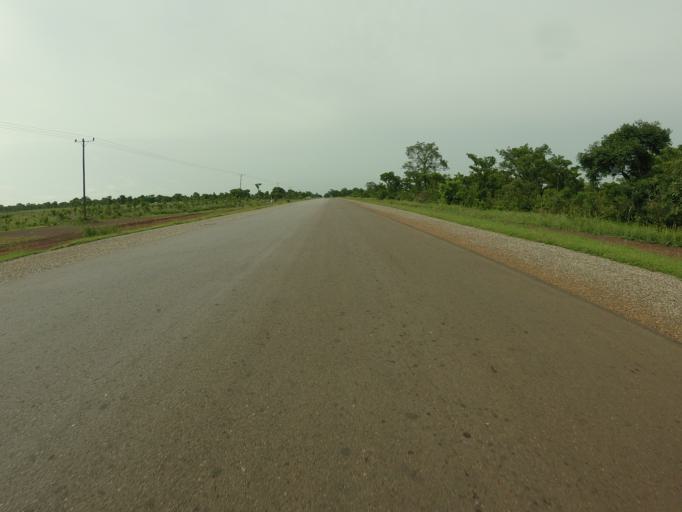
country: GH
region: Northern
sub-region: Yendi
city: Yendi
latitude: 9.6454
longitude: -0.0677
